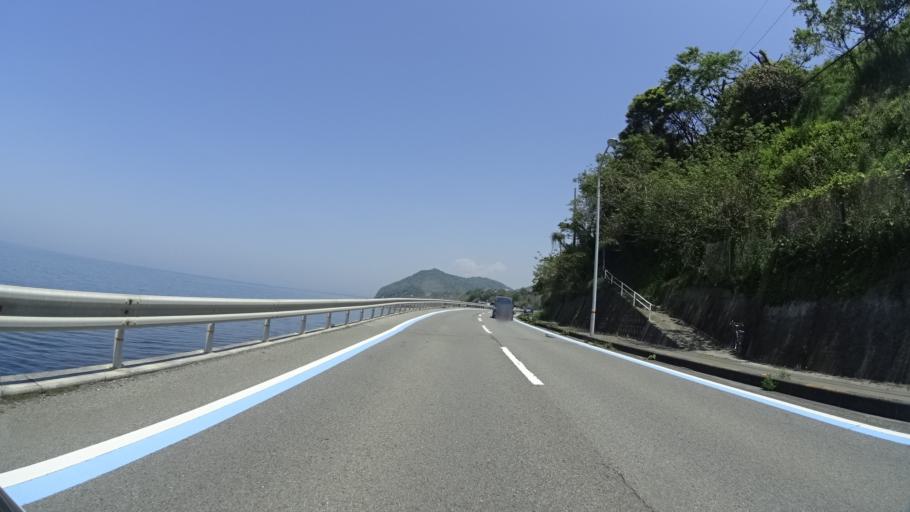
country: JP
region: Ehime
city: Iyo
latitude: 33.7014
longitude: 132.6571
